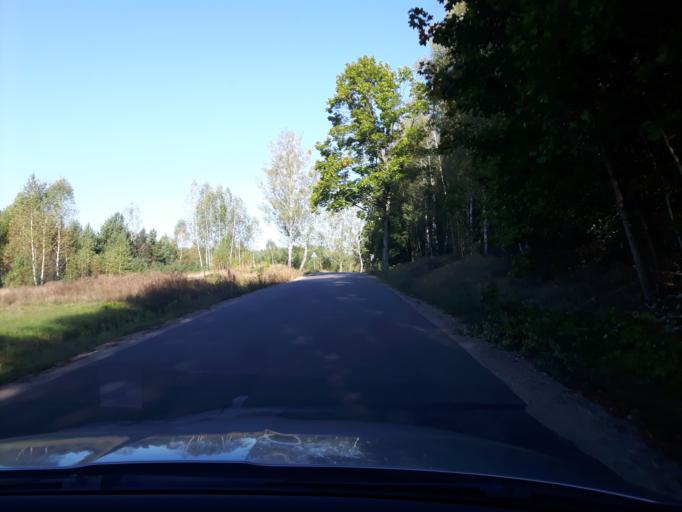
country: PL
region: Warmian-Masurian Voivodeship
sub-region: Powiat olsztynski
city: Gietrzwald
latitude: 53.7154
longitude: 20.2039
